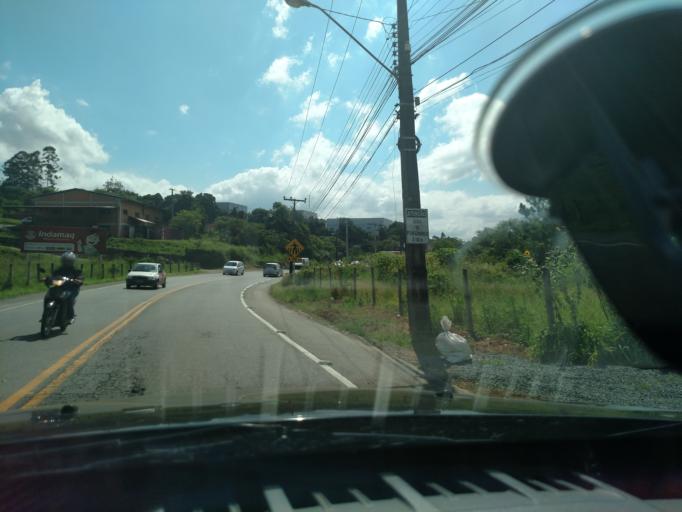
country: BR
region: Santa Catarina
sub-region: Indaial
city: Indaial
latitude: -26.8854
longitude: -49.1709
